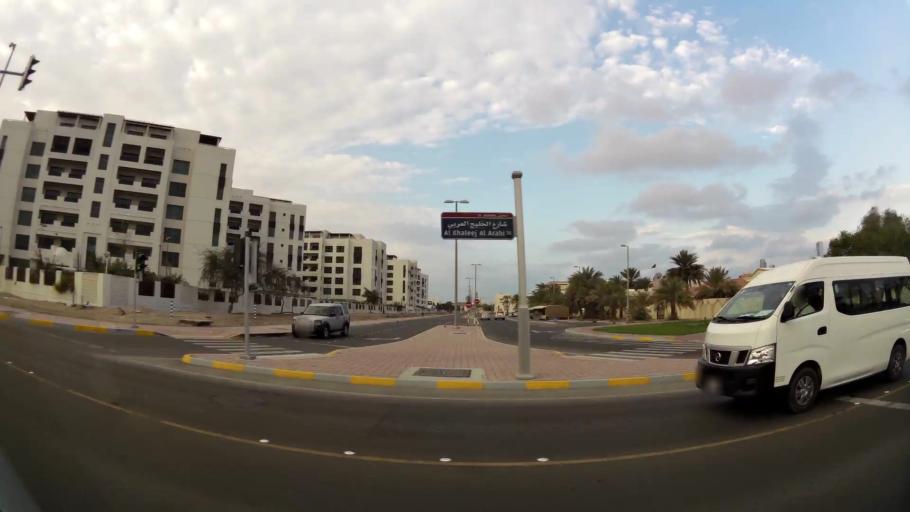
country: AE
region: Abu Dhabi
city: Abu Dhabi
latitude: 24.4601
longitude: 54.3518
